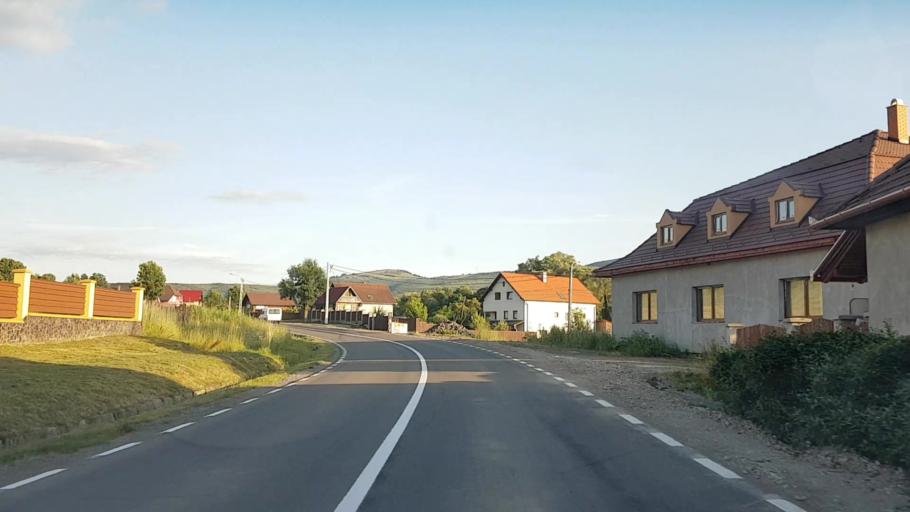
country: RO
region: Harghita
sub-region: Comuna Corund
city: Corund
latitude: 46.4895
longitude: 25.1686
